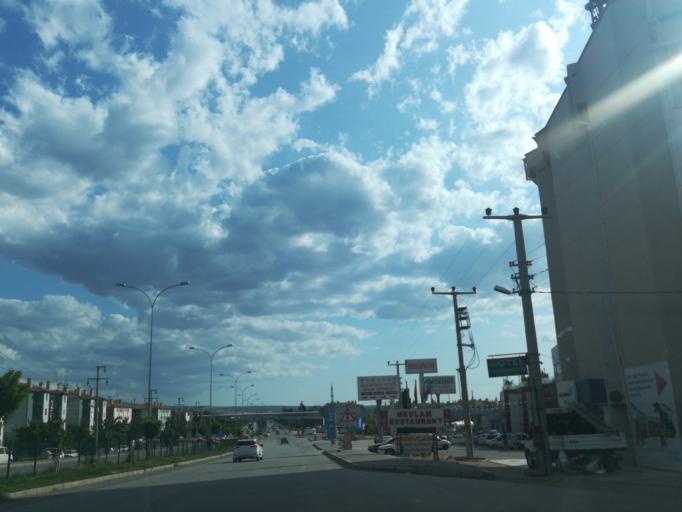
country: TR
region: Afyonkarahisar
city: Dinar
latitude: 38.0662
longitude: 30.1668
